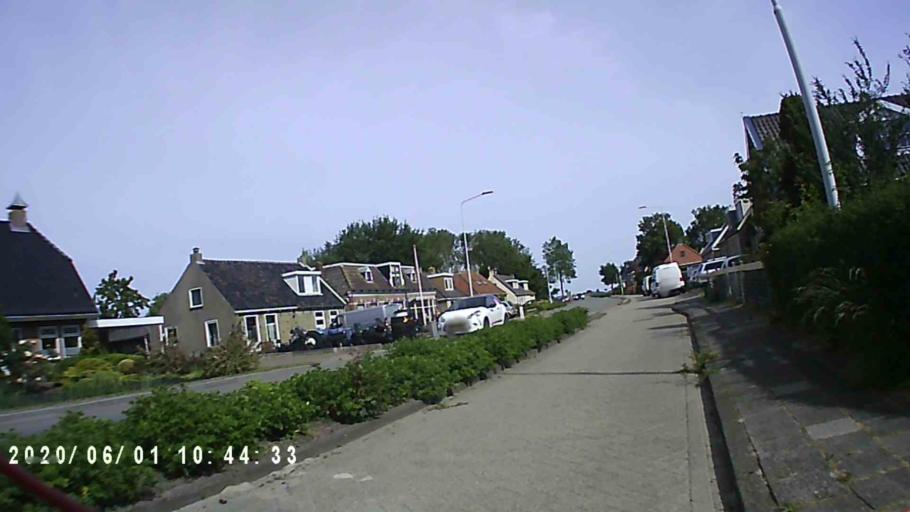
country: NL
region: Friesland
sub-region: Gemeente Franekeradeel
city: Franeker
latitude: 53.2082
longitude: 5.5424
